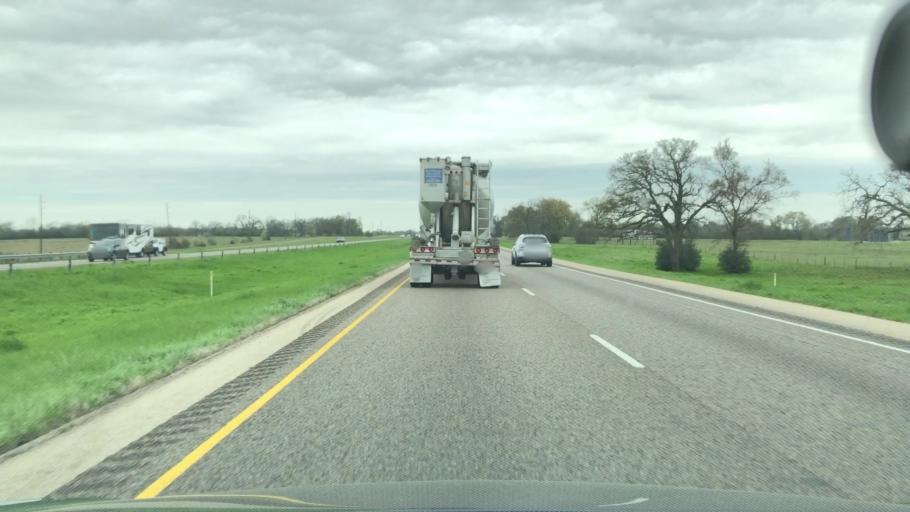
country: US
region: Texas
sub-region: Madison County
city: Madisonville
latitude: 31.0520
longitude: -95.9469
